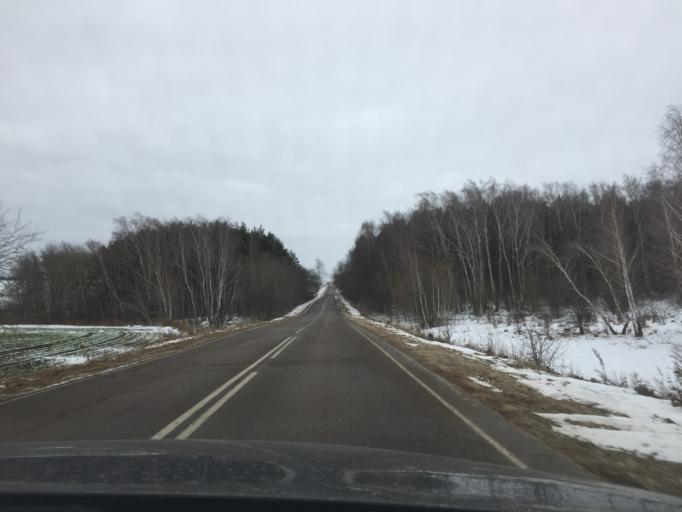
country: RU
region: Tula
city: Shchekino
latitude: 53.8108
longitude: 37.5412
